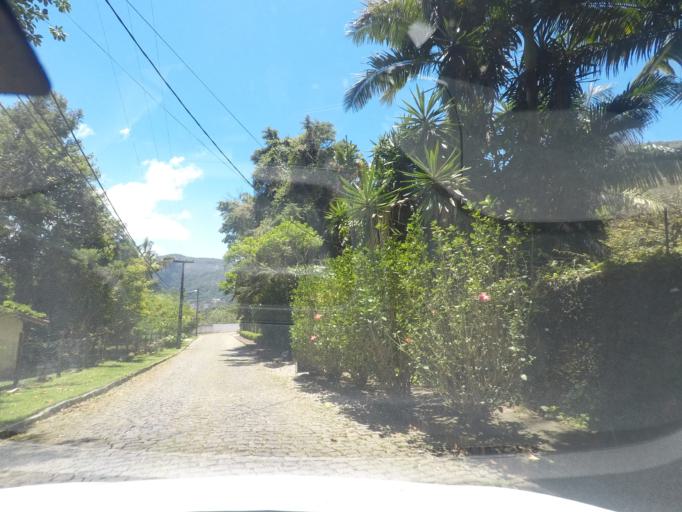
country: BR
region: Rio de Janeiro
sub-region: Teresopolis
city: Teresopolis
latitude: -22.4317
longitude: -42.9947
